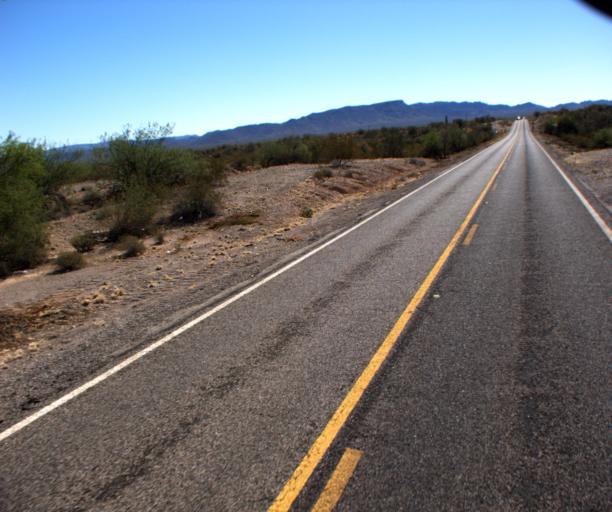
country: US
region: Arizona
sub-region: Pima County
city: Ajo
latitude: 32.3513
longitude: -112.8191
